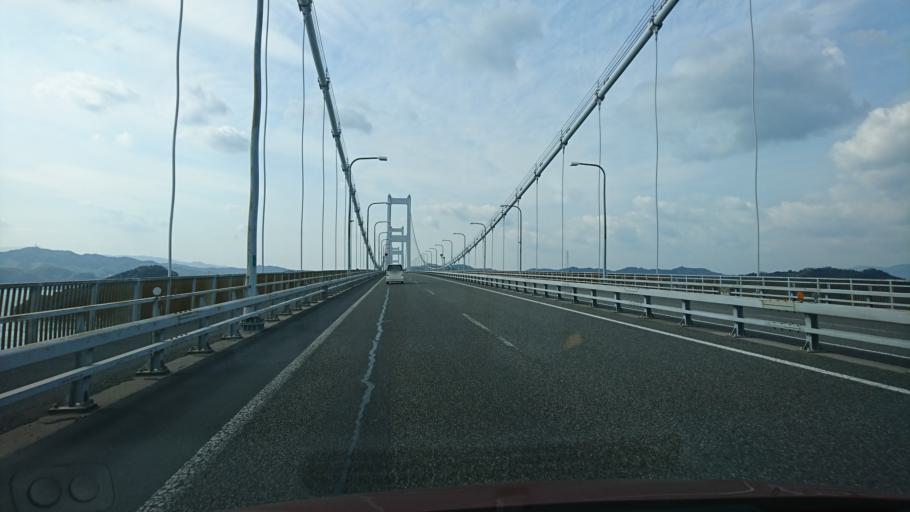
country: JP
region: Hiroshima
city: Takehara
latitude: 34.1220
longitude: 133.0027
